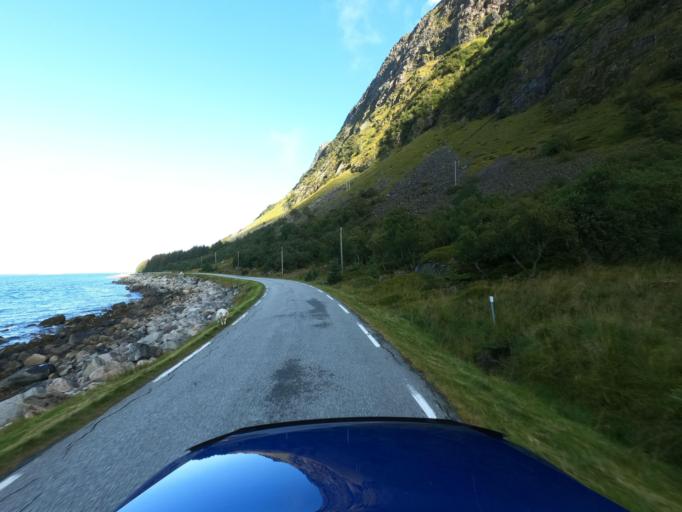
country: NO
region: Nordland
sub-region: Vagan
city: Kabelvag
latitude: 68.3110
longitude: 14.3136
